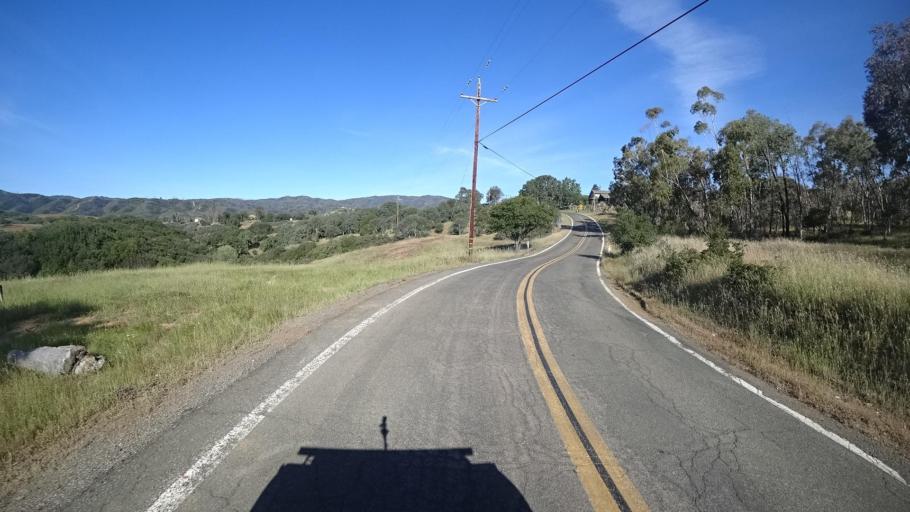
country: US
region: California
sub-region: Lake County
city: Lakeport
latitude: 39.0411
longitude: -122.9487
